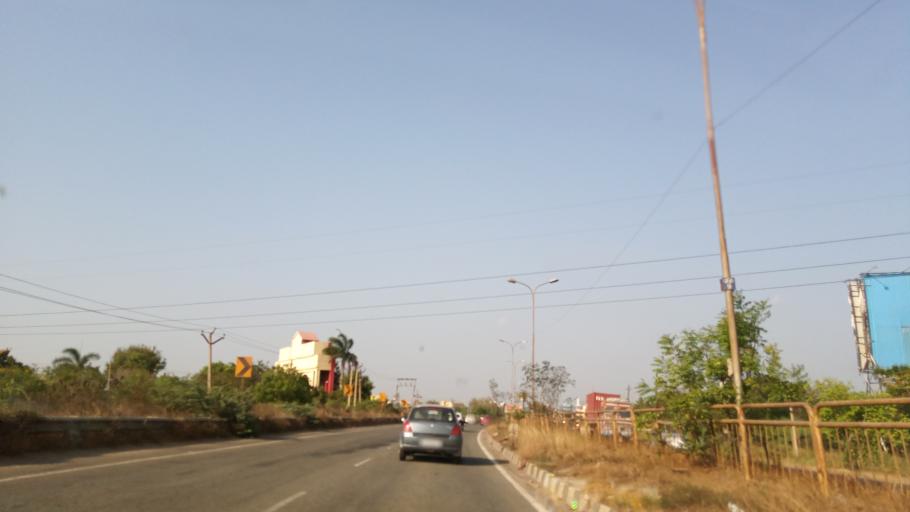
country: IN
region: Tamil Nadu
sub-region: Kancheepuram
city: Sriperumbudur
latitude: 13.0118
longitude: 79.9992
